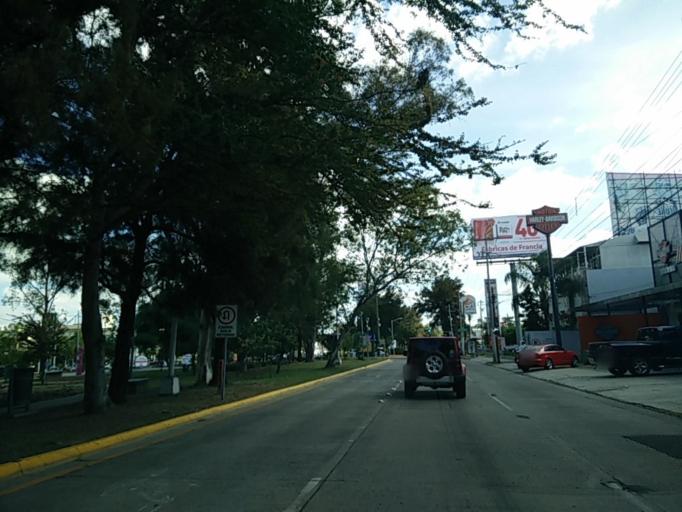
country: MX
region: Jalisco
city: Guadalajara
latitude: 20.6710
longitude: -103.4059
